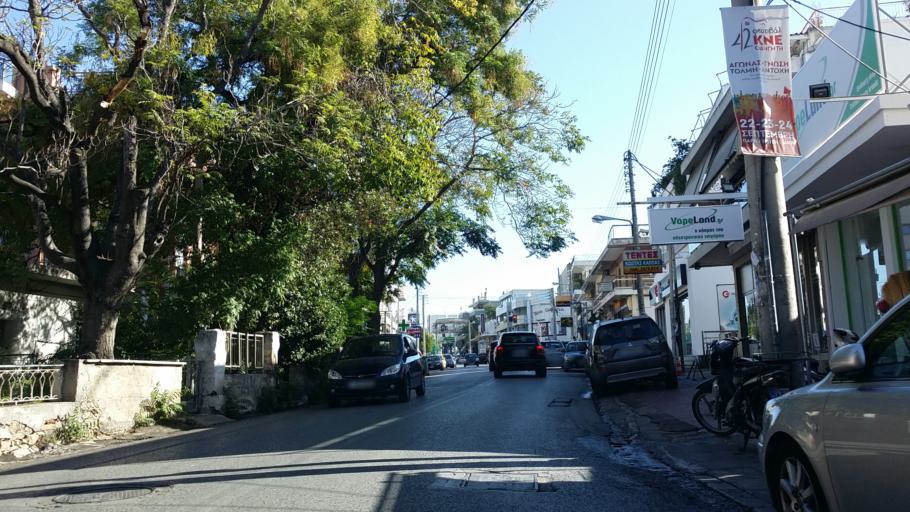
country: GR
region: Attica
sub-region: Nomarchia Athinas
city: Irakleio
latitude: 38.0493
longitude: 23.7628
